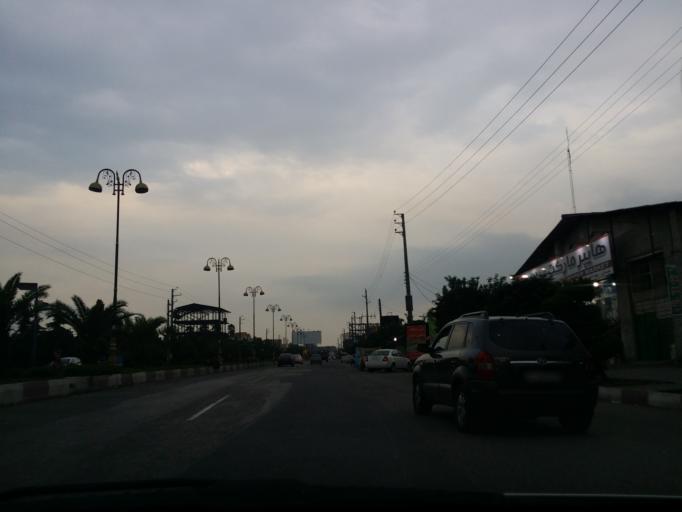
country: IR
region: Mazandaran
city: `Abbasabad
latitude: 36.7272
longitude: 51.1131
